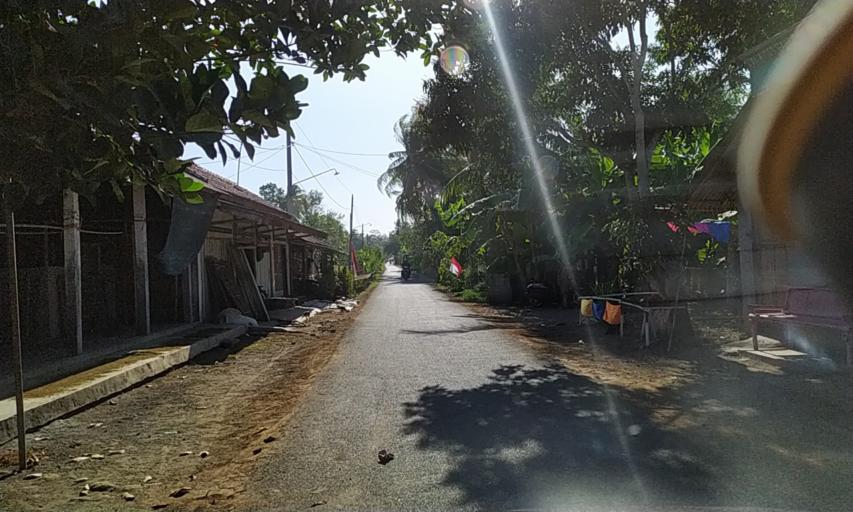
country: ID
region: Central Java
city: Sidaurip
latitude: -7.5259
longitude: 108.7479
